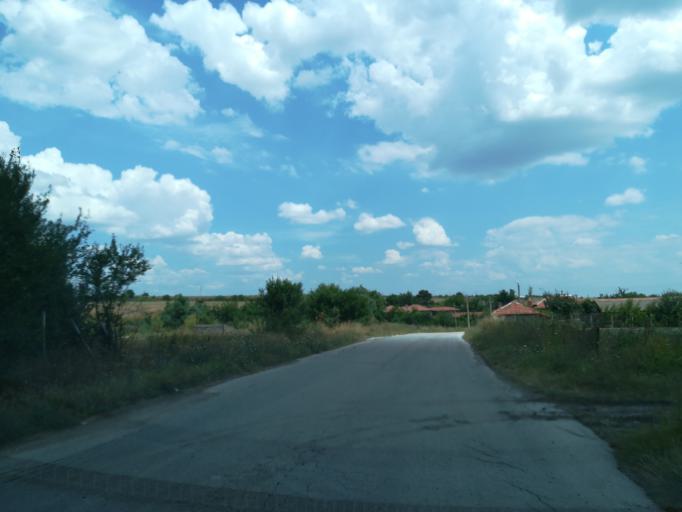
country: BG
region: Khaskovo
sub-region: Obshtina Mineralni Bani
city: Mineralni Bani
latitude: 41.9874
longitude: 25.1762
